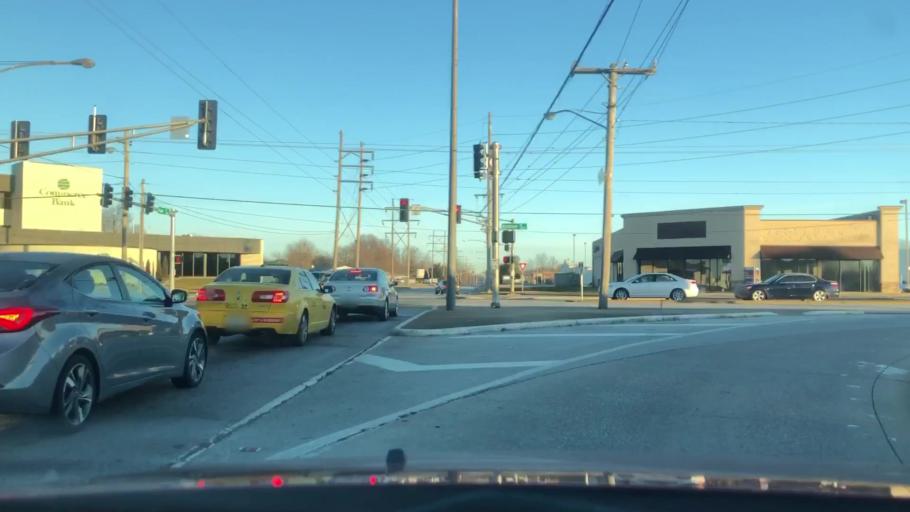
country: US
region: Missouri
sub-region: Greene County
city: Springfield
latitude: 37.1592
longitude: -93.2716
